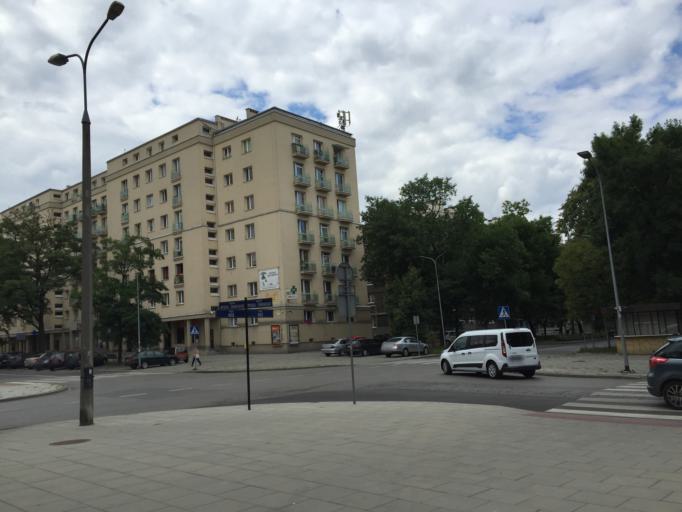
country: PL
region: Lesser Poland Voivodeship
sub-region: Powiat wielicki
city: Kokotow
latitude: 50.0764
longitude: 20.0391
